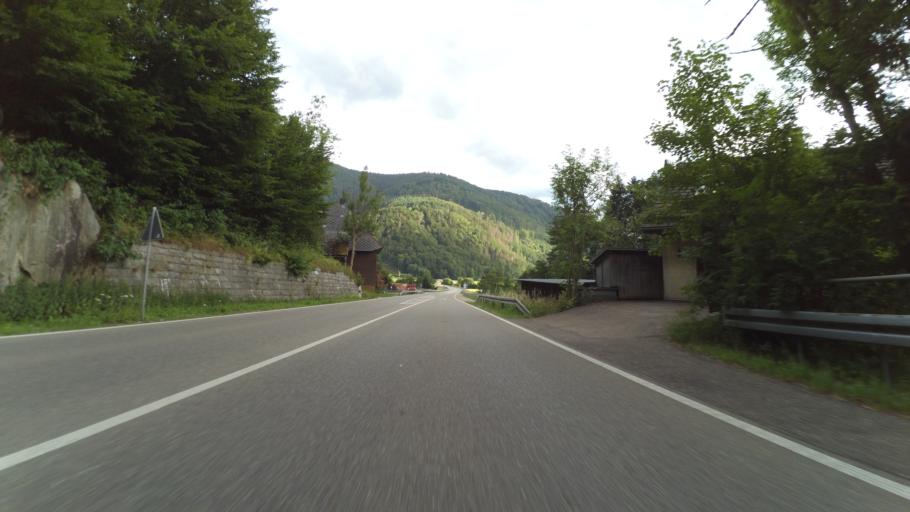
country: DE
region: Baden-Wuerttemberg
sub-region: Freiburg Region
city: Utzenfeld
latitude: 47.8087
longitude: 7.9359
